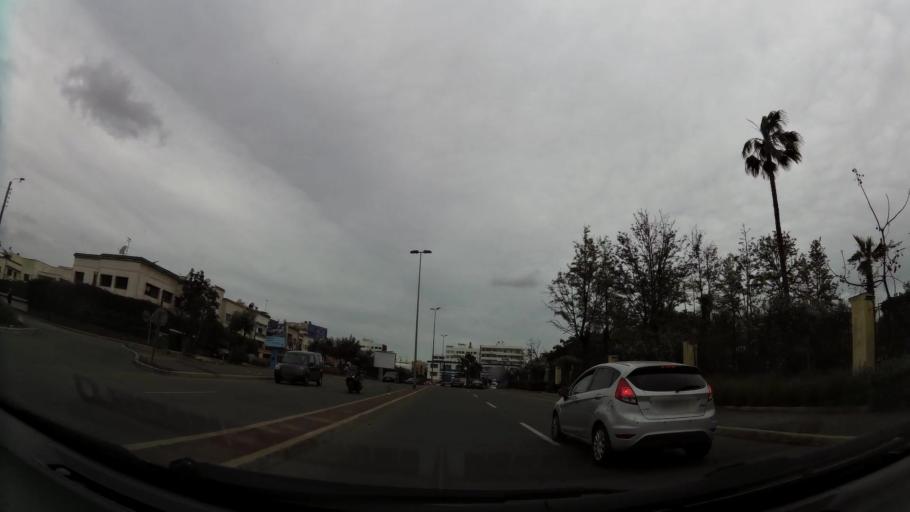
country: MA
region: Grand Casablanca
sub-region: Casablanca
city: Casablanca
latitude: 33.5676
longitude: -7.6155
